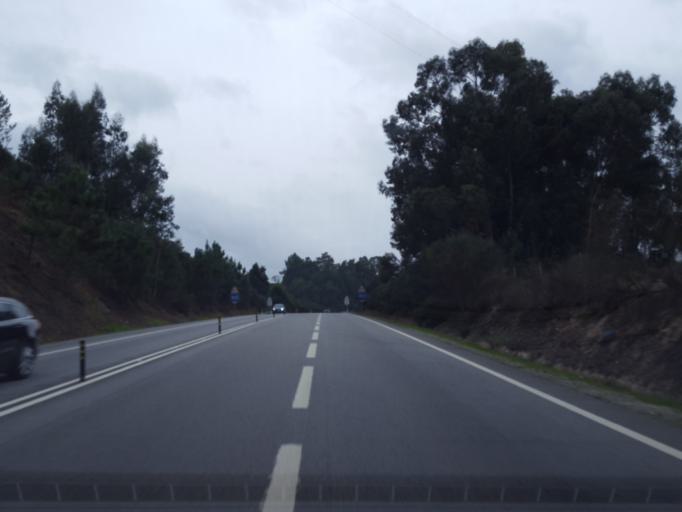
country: PT
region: Porto
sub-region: Marco de Canaveses
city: Marco de Canavezes
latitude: 41.2277
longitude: -8.1962
